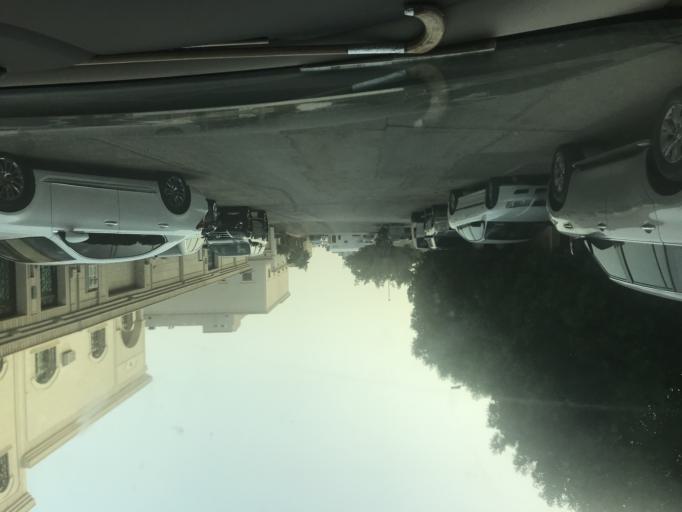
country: SA
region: Ar Riyad
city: Riyadh
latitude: 24.7403
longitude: 46.7553
